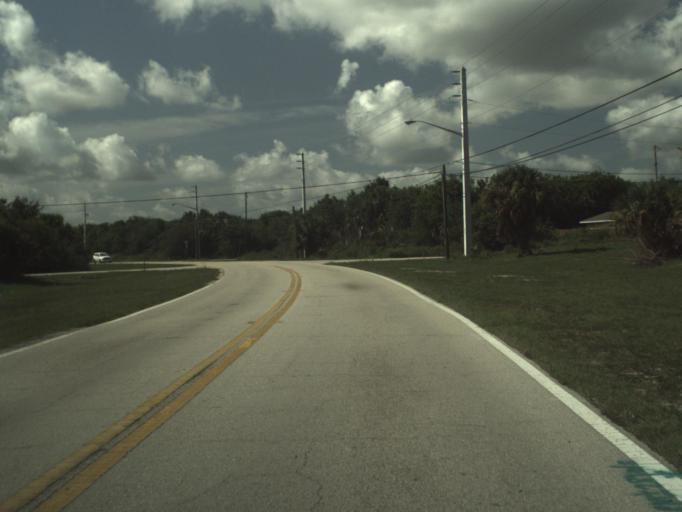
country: US
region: Florida
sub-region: Saint Lucie County
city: Port Saint Lucie
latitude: 27.2335
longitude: -80.3770
